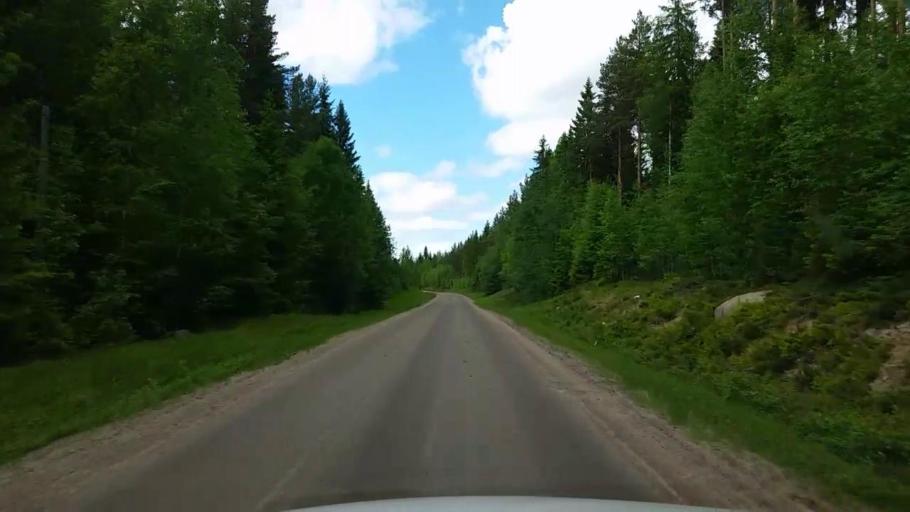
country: SE
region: Gaevleborg
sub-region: Ovanakers Kommun
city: Alfta
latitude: 61.4926
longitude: 15.9830
